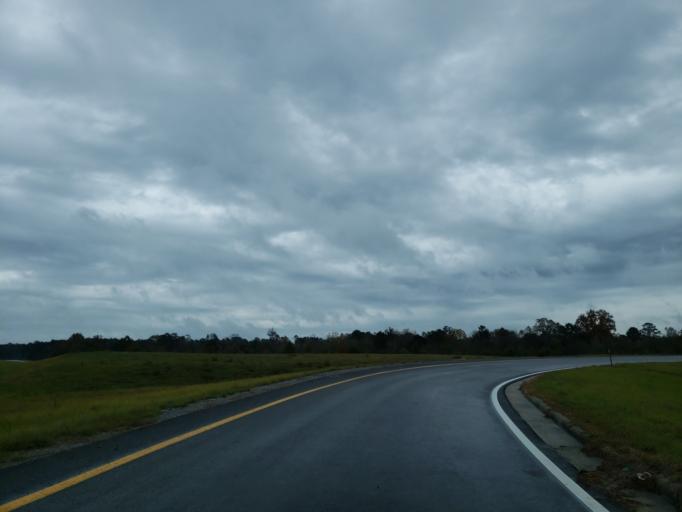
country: US
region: Mississippi
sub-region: Wayne County
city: Waynesboro
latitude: 31.7079
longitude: -88.6246
